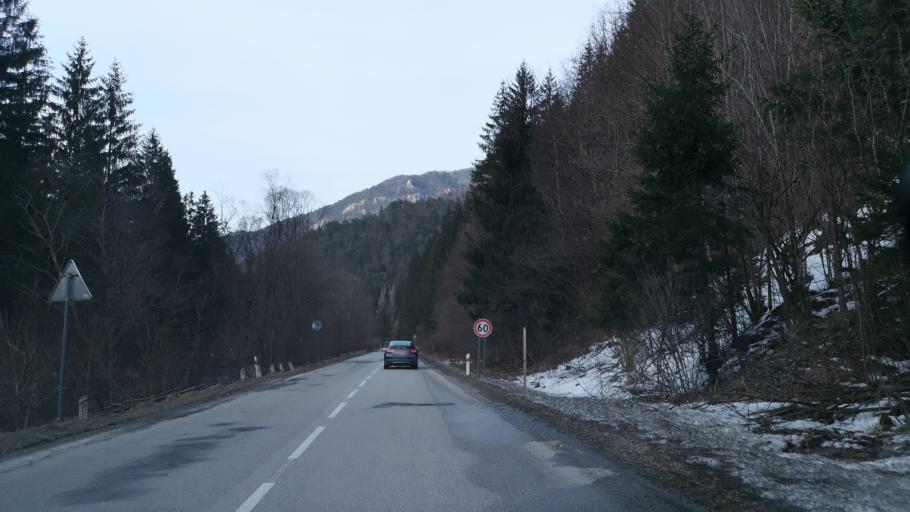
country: SK
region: Zilinsky
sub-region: Okres Dolny Kubin
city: Dolny Kubin
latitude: 49.2101
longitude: 19.1651
